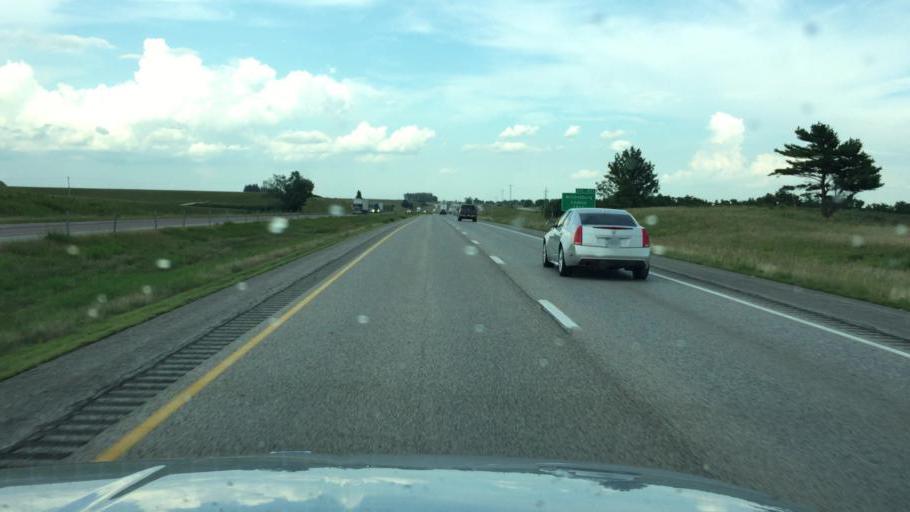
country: US
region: Iowa
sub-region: Iowa County
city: Marengo
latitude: 41.6961
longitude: -92.1873
